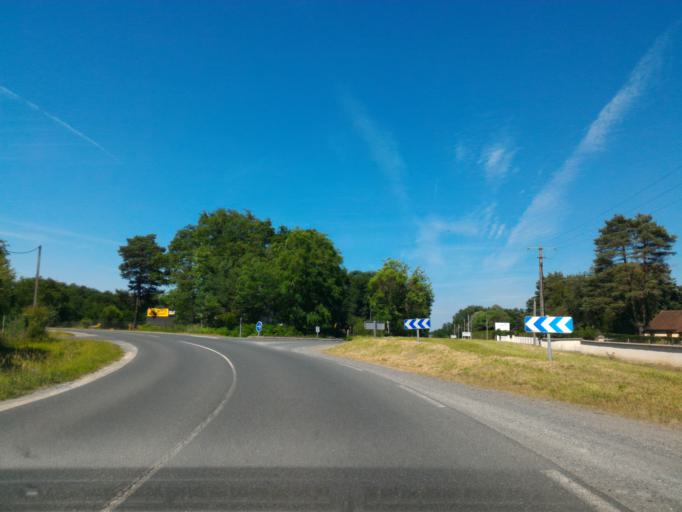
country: FR
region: Centre
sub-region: Departement de l'Indre
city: Luant
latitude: 46.7402
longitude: 1.6176
